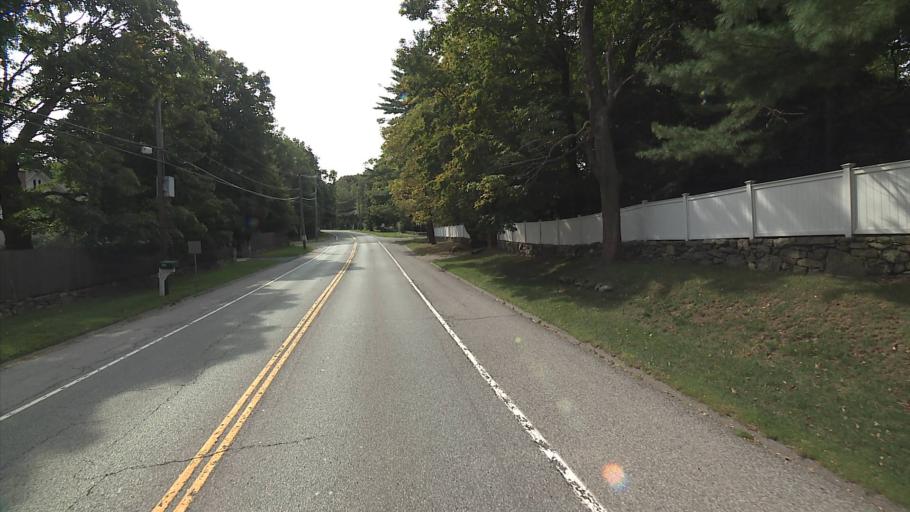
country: US
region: Connecticut
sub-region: Fairfield County
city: New Canaan
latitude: 41.1861
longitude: -73.5043
